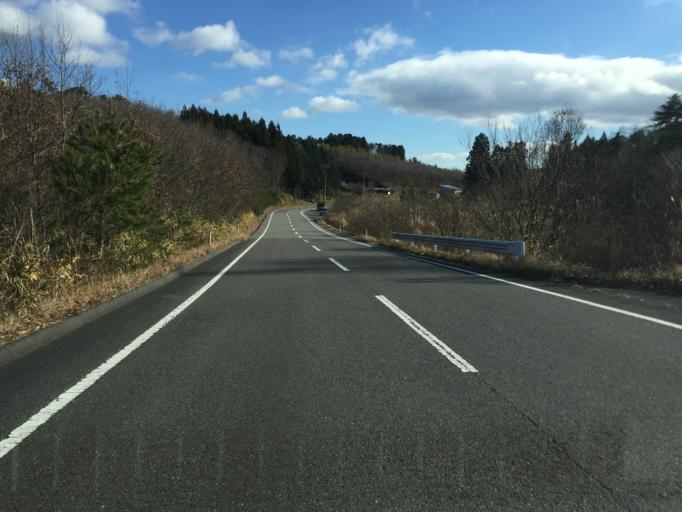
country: JP
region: Fukushima
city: Ishikawa
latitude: 37.2514
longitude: 140.5526
